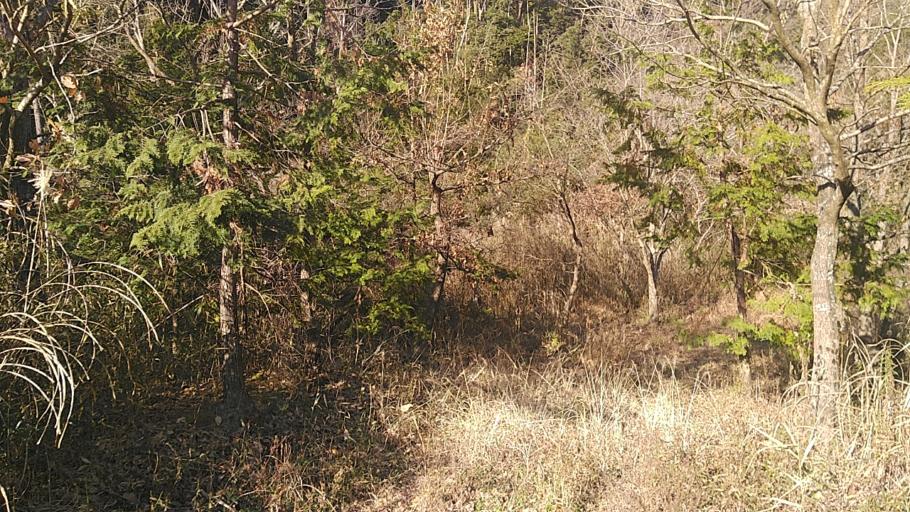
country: JP
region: Chiba
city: Kimitsu
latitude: 35.2845
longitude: 139.9628
